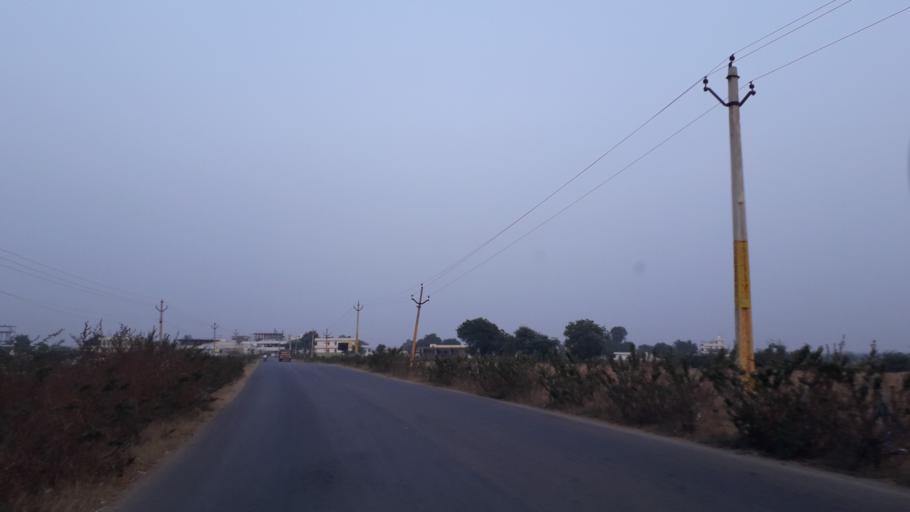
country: IN
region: Telangana
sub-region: Medak
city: Patancheru
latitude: 17.5134
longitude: 78.2276
